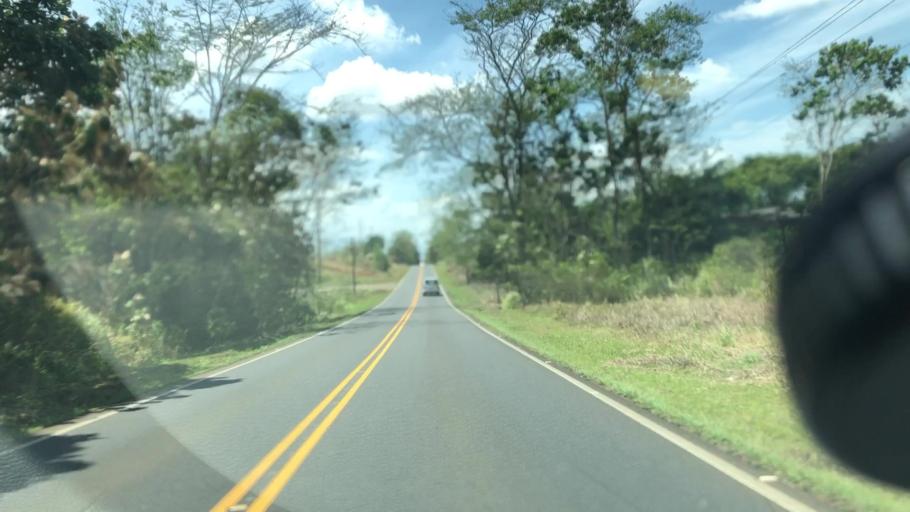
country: CR
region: Alajuela
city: Pital
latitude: 10.4577
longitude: -84.3973
